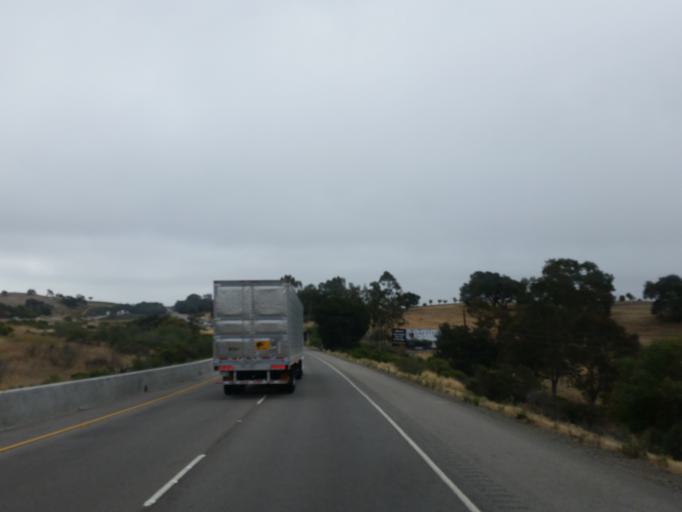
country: US
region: California
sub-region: San Luis Obispo County
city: Arroyo Grande
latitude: 35.0920
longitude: -120.5424
